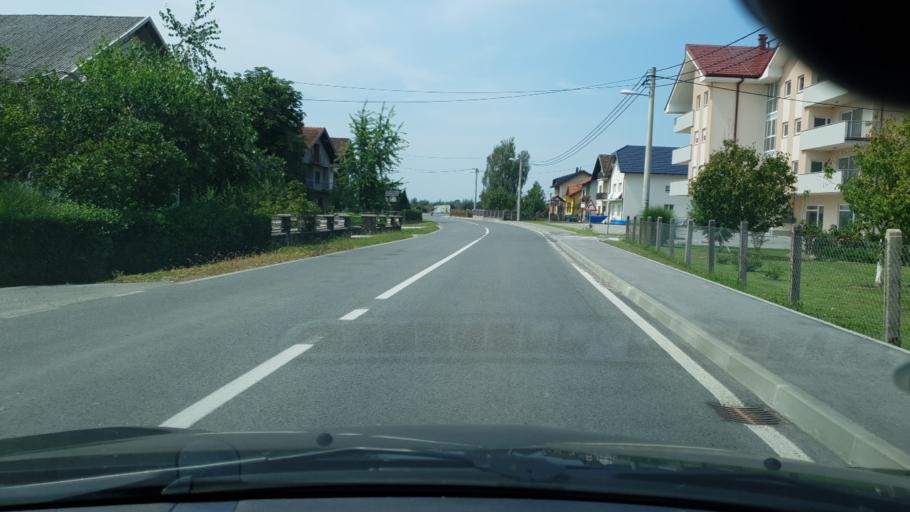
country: HR
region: Krapinsko-Zagorska
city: Bedekovcina
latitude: 46.0367
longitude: 15.9796
